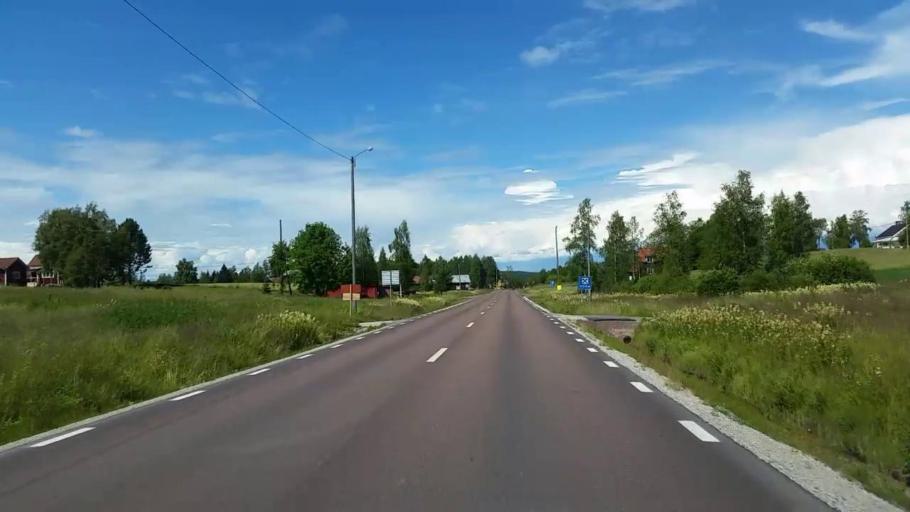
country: SE
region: Dalarna
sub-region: Rattviks Kommun
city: Raettvik
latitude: 61.0387
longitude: 15.1984
